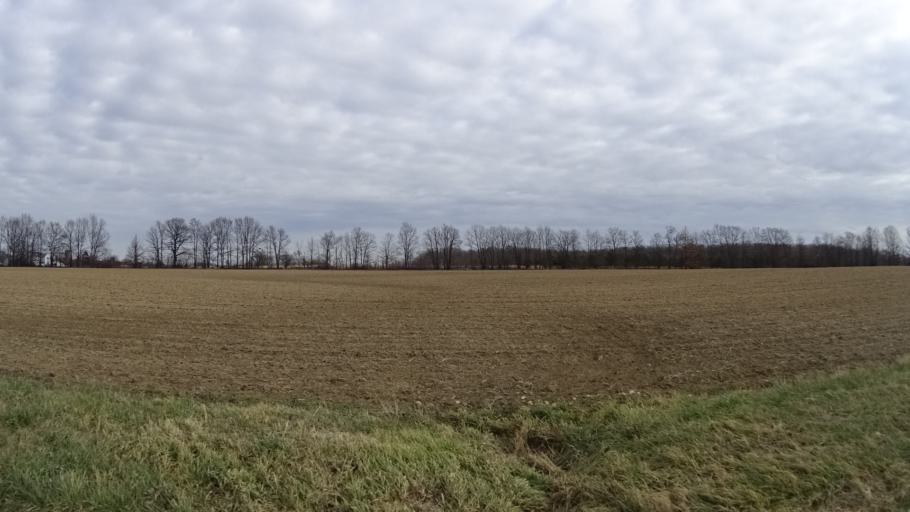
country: US
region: Ohio
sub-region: Lorain County
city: Camden
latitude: 41.2117
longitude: -82.3356
